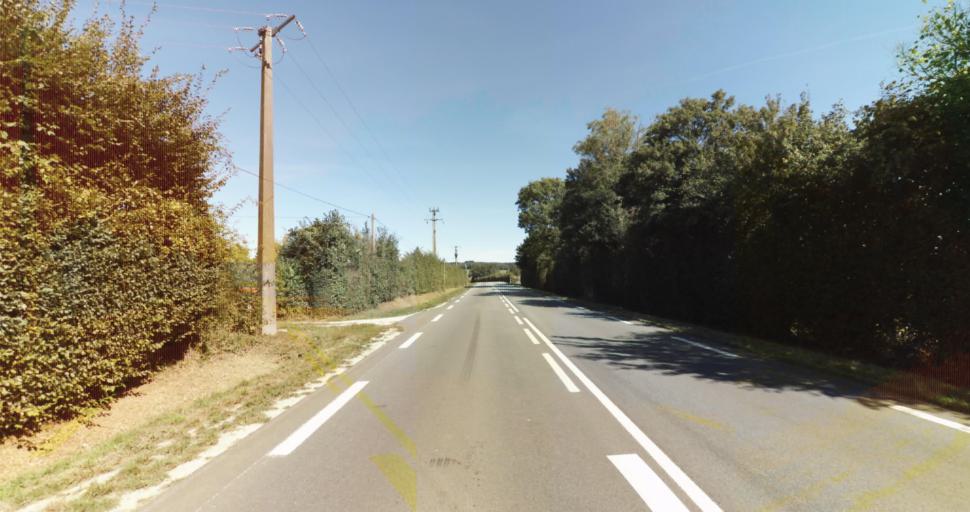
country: FR
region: Lower Normandy
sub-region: Departement de l'Orne
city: Gace
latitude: 48.7685
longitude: 0.2903
